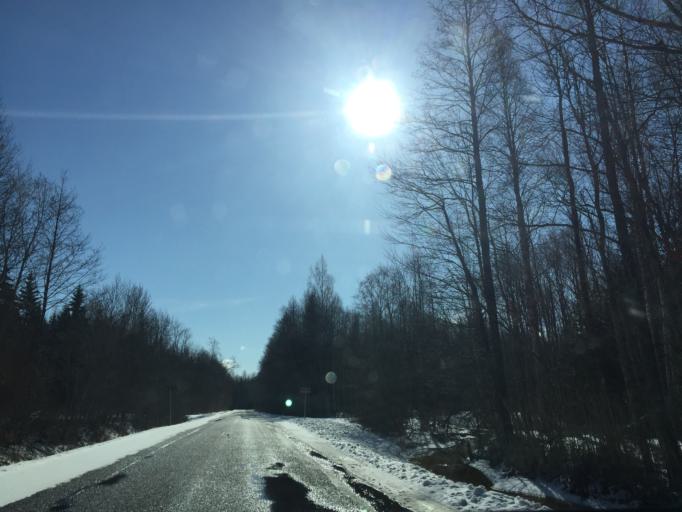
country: LV
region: Salacgrivas
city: Ainazi
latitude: 58.0089
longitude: 24.4956
